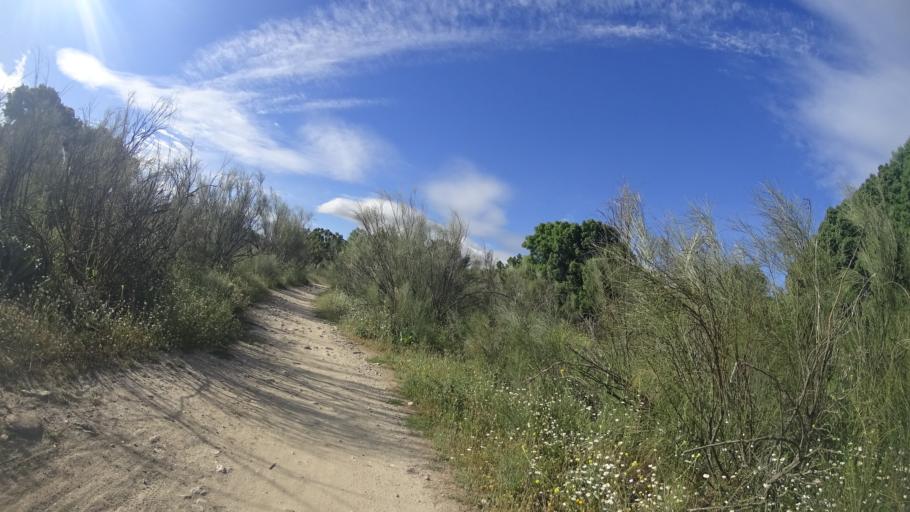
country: ES
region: Madrid
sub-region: Provincia de Madrid
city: Villanueva del Pardillo
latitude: 40.5152
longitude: -3.9414
